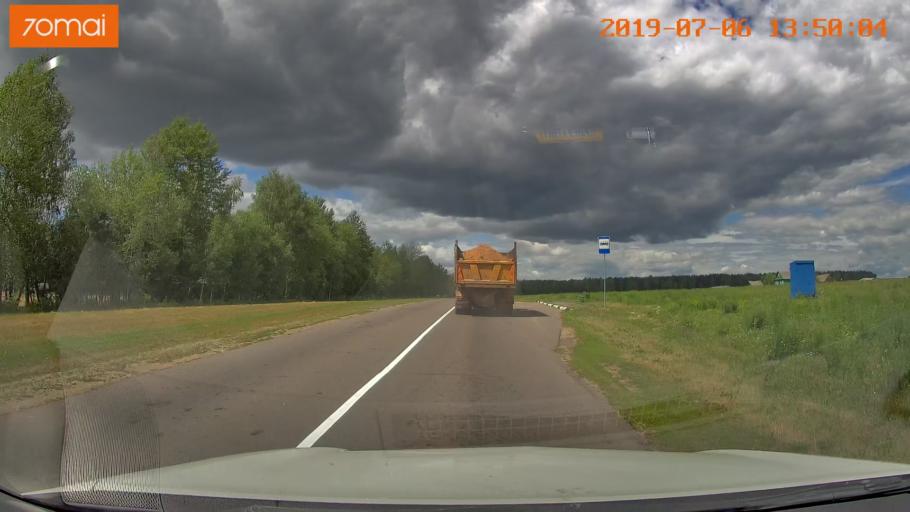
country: BY
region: Minsk
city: Ivyanyets
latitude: 53.6969
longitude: 26.8475
